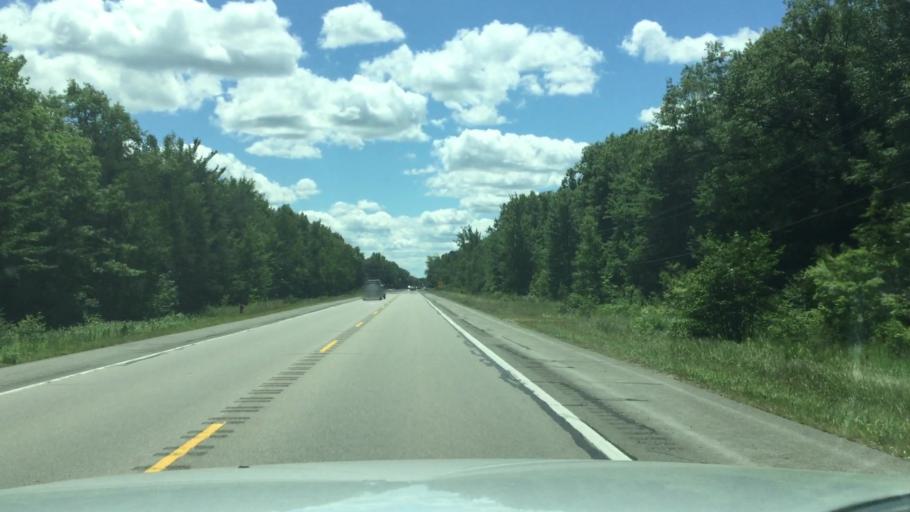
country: US
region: Michigan
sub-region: Saginaw County
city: Shields
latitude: 43.3853
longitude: -84.1312
